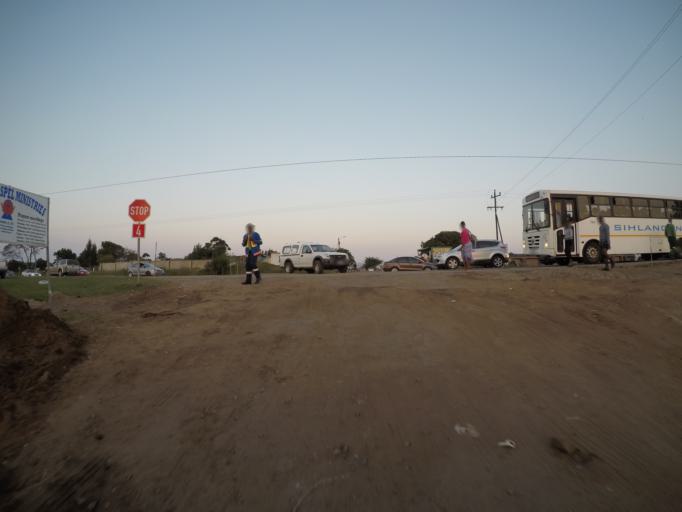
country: ZA
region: KwaZulu-Natal
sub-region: uThungulu District Municipality
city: Richards Bay
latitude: -28.7580
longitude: 32.1335
